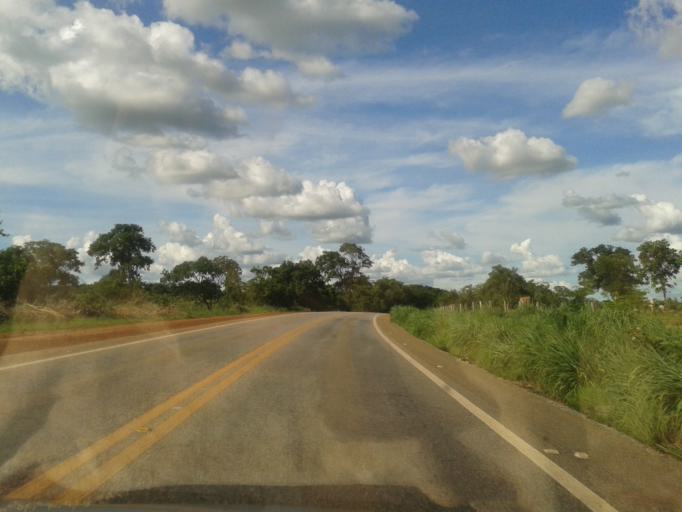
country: BR
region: Goias
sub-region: Mozarlandia
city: Mozarlandia
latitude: -14.6987
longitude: -50.5459
